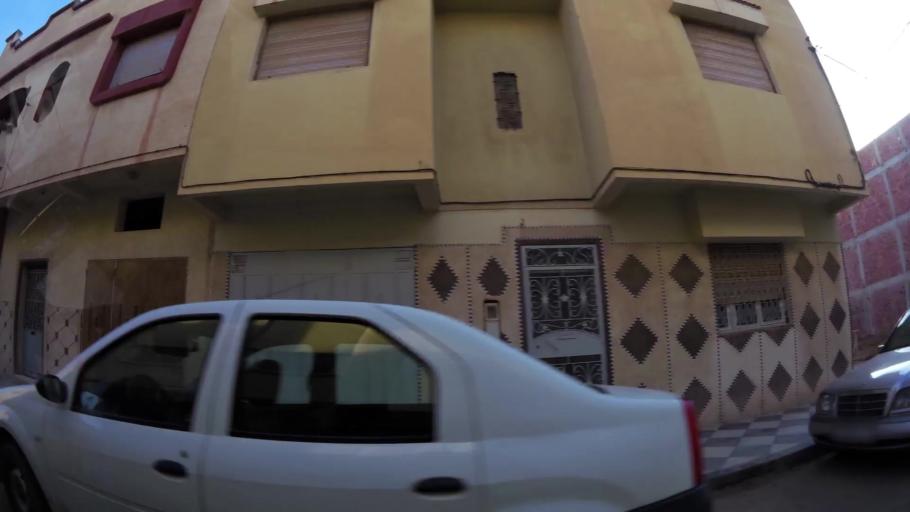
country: MA
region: Oriental
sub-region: Oujda-Angad
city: Oujda
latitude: 34.6779
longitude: -1.8900
